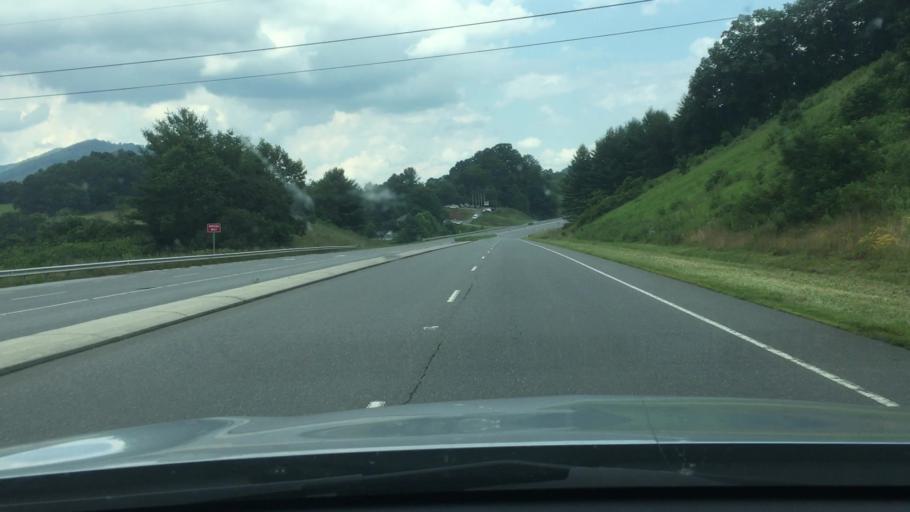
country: US
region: North Carolina
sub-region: Yancey County
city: Burnsville
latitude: 35.9109
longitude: -82.3719
